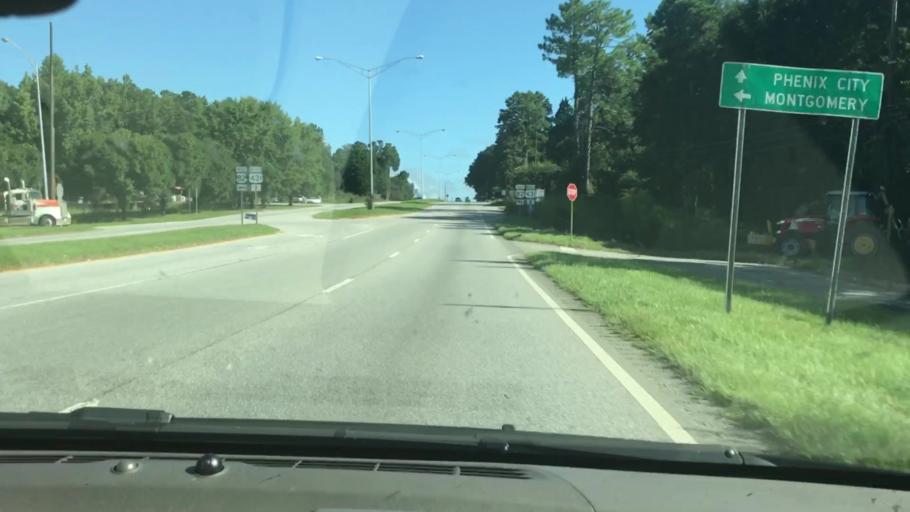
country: US
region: Alabama
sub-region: Barbour County
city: Eufaula
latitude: 31.9114
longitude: -85.1487
